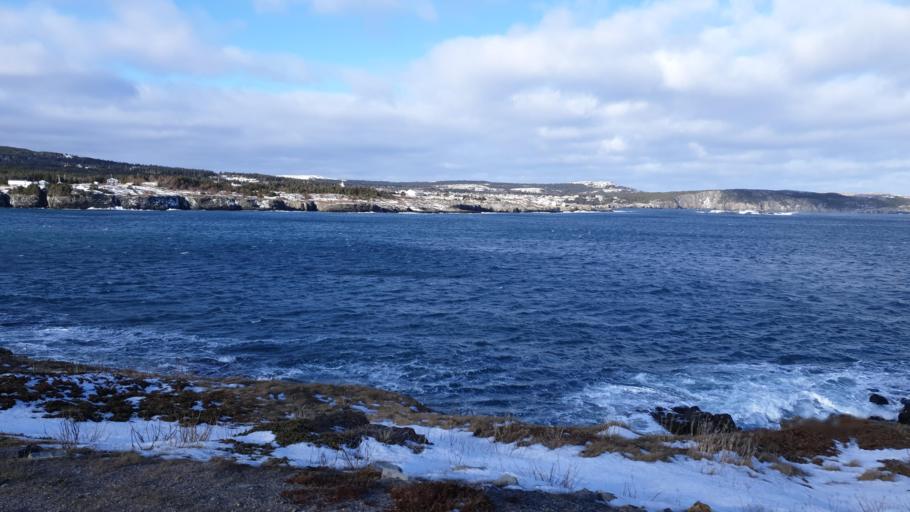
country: CA
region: Newfoundland and Labrador
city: Bonavista
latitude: 48.6255
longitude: -53.0256
